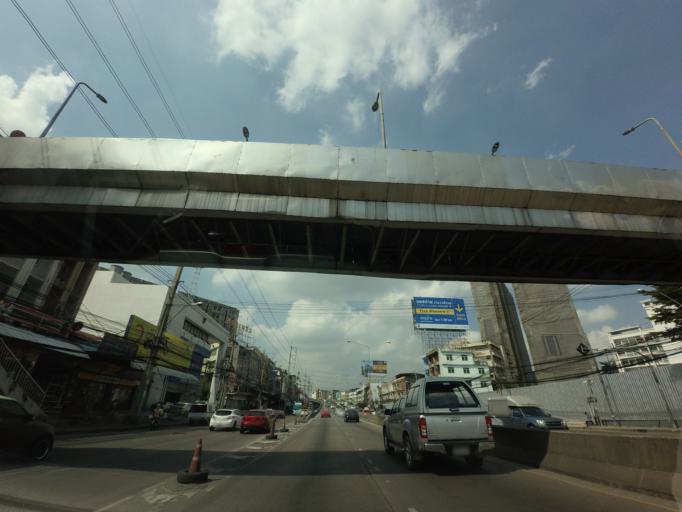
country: TH
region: Bangkok
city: Chatuchak
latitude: 13.8547
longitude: 100.5486
